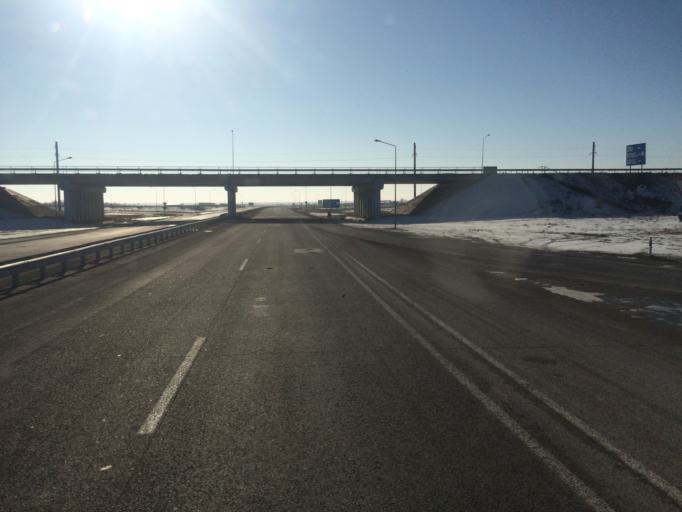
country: KG
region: Chuy
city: Sokuluk
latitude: 43.2764
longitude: 74.2313
